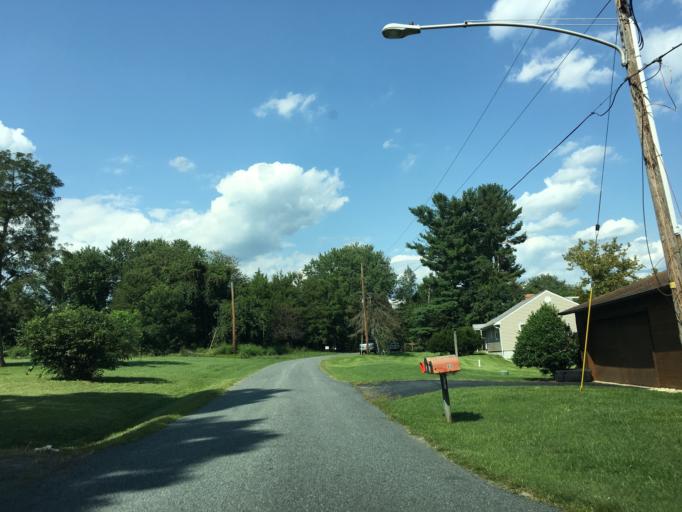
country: US
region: Maryland
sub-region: Cecil County
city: North East
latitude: 39.5199
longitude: -75.8965
